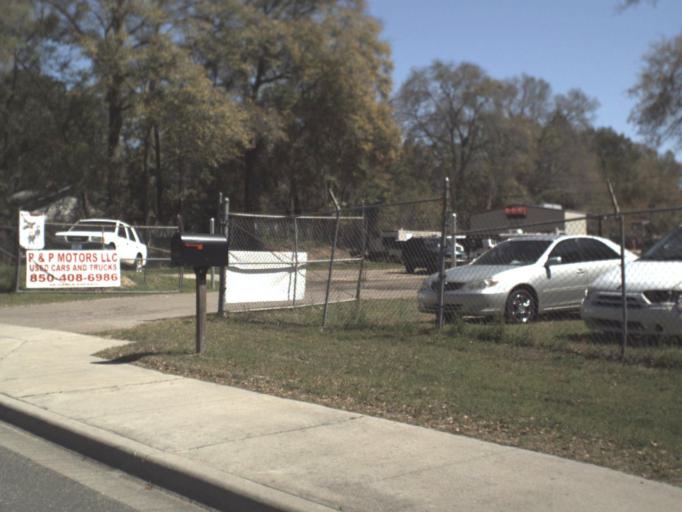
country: US
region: Florida
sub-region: Leon County
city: Tallahassee
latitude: 30.3940
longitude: -84.2834
